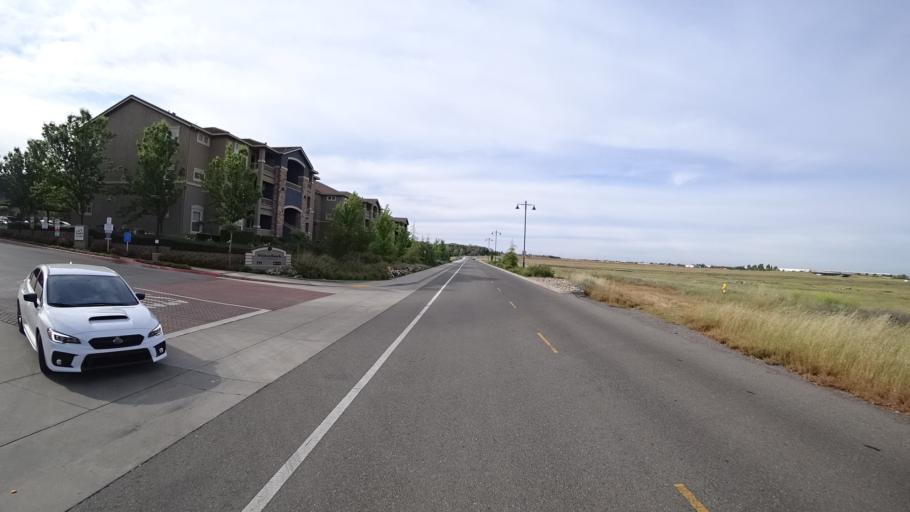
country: US
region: California
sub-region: Placer County
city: Lincoln
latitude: 38.8365
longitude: -121.2926
